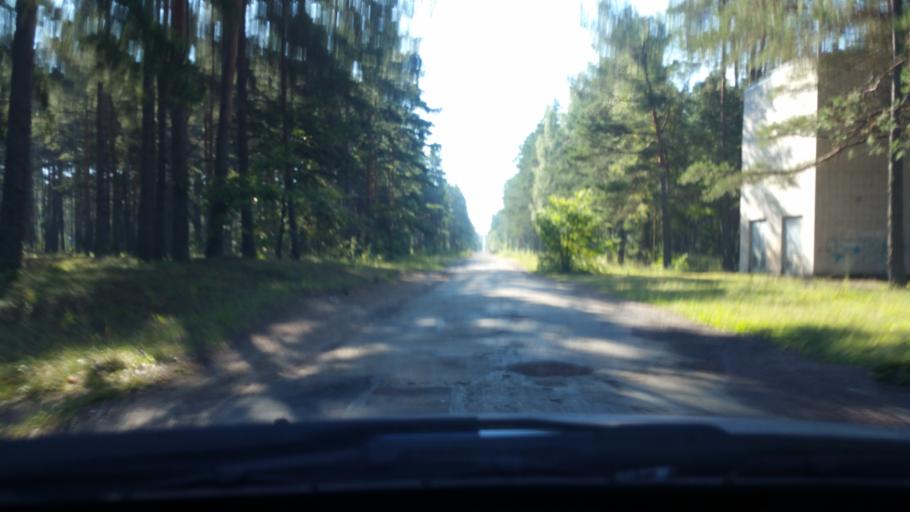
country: LV
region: Adazi
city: Adazi
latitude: 57.0986
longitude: 24.3522
